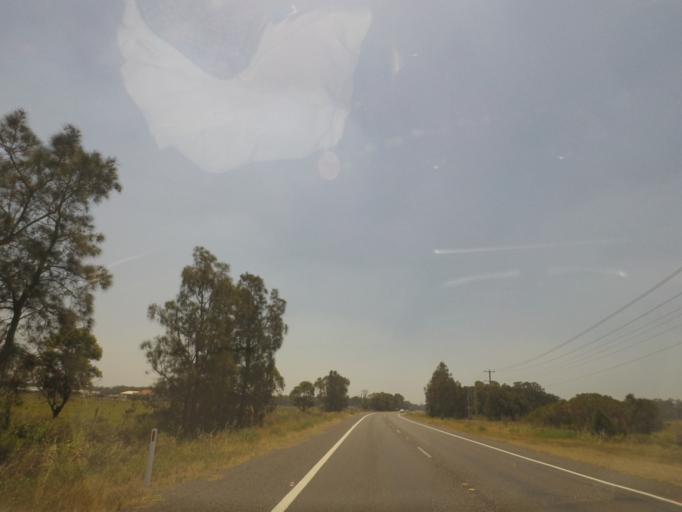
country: AU
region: New South Wales
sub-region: Port Stephens Shire
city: Medowie
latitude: -32.7953
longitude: 151.8938
